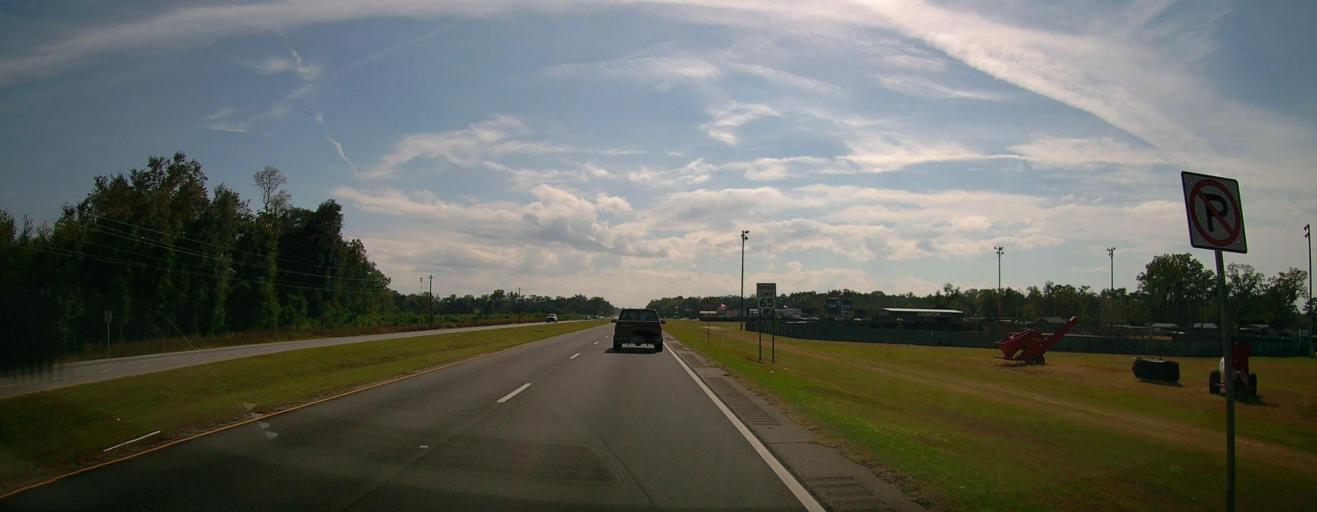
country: US
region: Georgia
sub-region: Dougherty County
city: Putney
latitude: 31.3793
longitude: -84.1504
